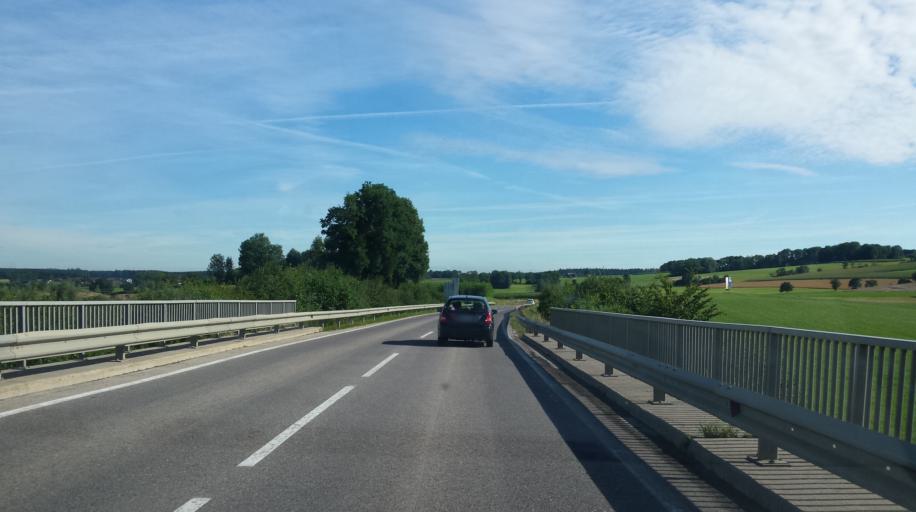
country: AT
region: Upper Austria
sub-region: Politischer Bezirk Vocklabruck
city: Sankt Georgen im Attergau
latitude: 47.9309
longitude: 13.5025
